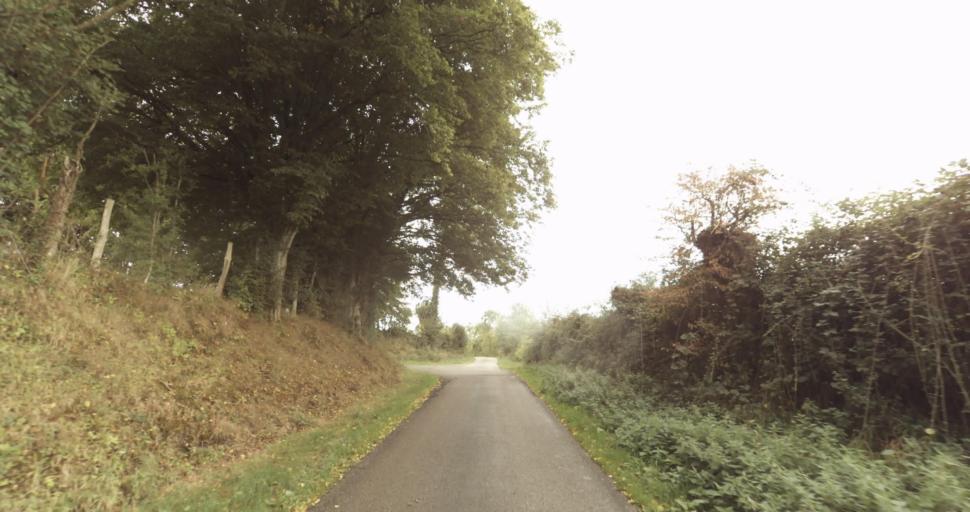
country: FR
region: Lower Normandy
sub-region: Departement de l'Orne
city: Gace
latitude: 48.8039
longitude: 0.2749
